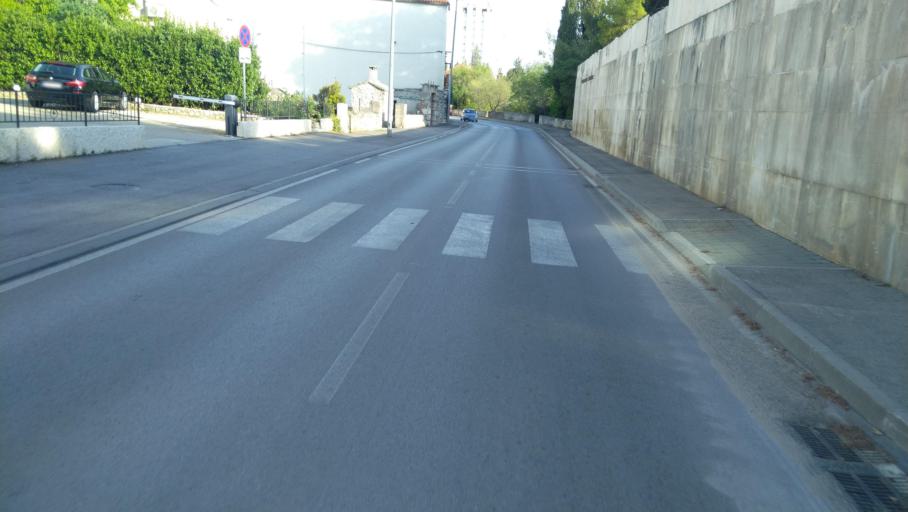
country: HR
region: Sibensko-Kniniska
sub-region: Grad Sibenik
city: Sibenik
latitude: 43.7429
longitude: 15.8978
